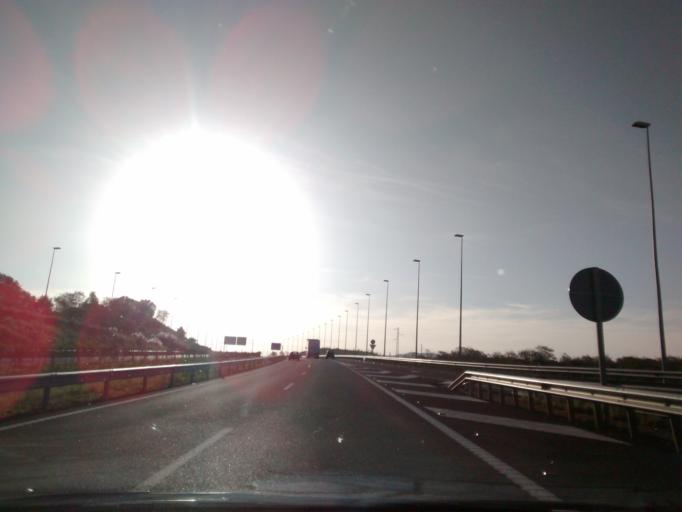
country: ES
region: Cantabria
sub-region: Provincia de Cantabria
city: El Astillero
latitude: 43.3905
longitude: -3.8339
